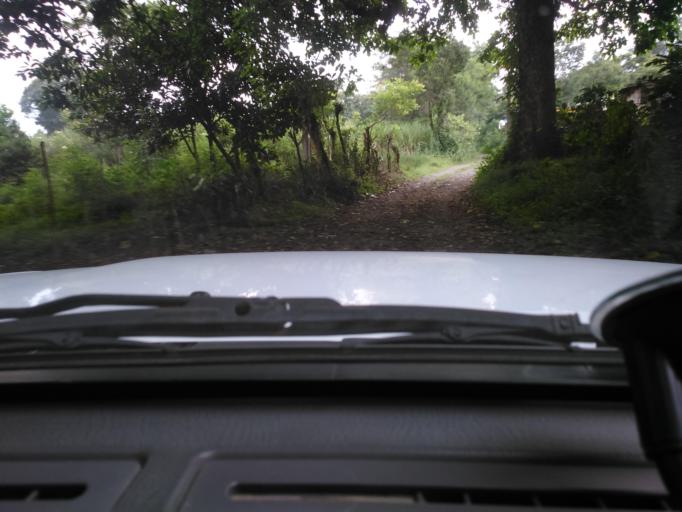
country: MX
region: Veracruz
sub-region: Mariano Escobedo
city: Chicola
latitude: 18.8957
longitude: -97.1096
